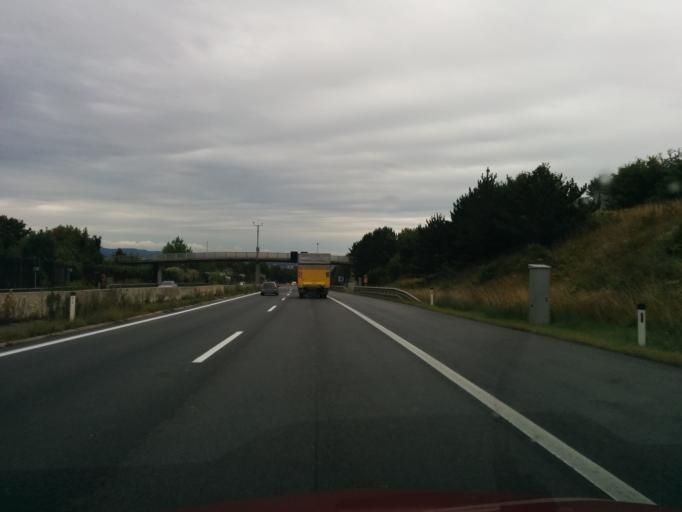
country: AT
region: Lower Austria
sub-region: Politischer Bezirk Modling
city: Perchtoldsdorf
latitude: 48.1051
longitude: 16.2577
